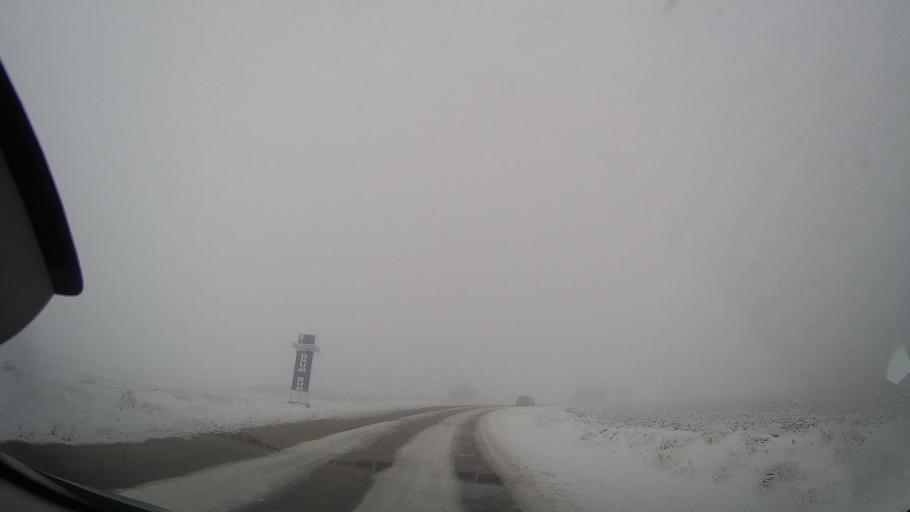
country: RO
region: Neamt
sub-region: Comuna Valea Ursului
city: Valea Ursului
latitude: 46.8258
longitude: 27.0620
